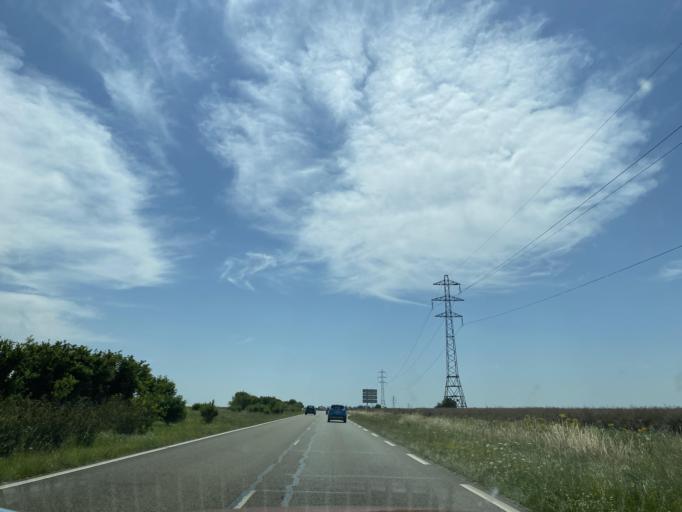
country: FR
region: Centre
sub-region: Departement d'Eure-et-Loir
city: Mainvilliers
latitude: 48.4650
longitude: 1.4640
